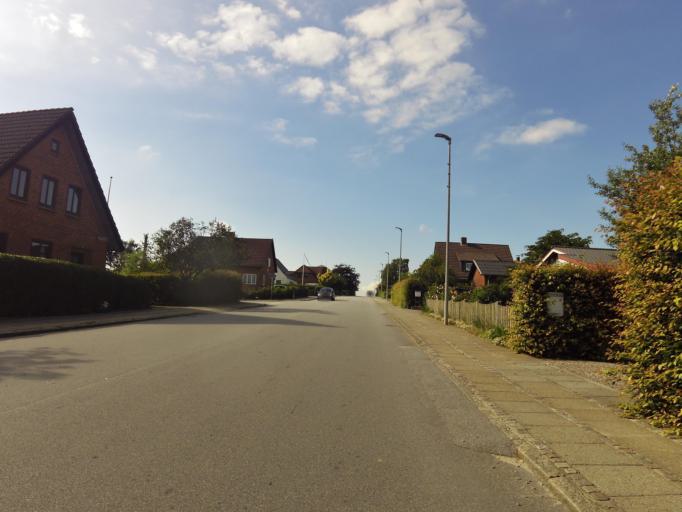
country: DK
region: South Denmark
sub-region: Vejen Kommune
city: Rodding
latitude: 55.3716
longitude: 9.0594
